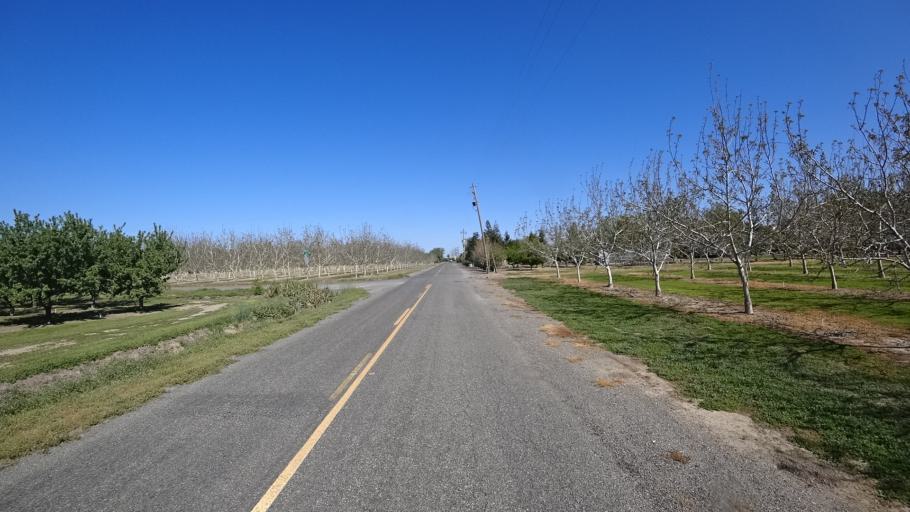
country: US
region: California
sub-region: Glenn County
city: Hamilton City
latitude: 39.7287
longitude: -122.0147
